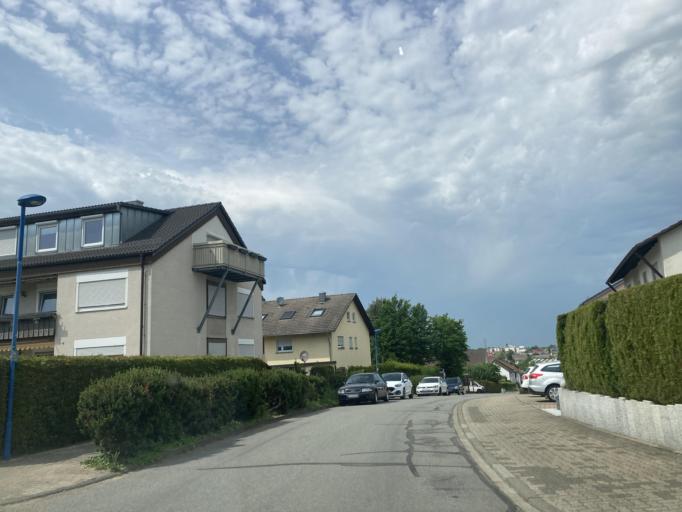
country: DE
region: Baden-Wuerttemberg
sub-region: Karlsruhe Region
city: Ettlingen
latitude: 48.9184
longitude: 8.4841
